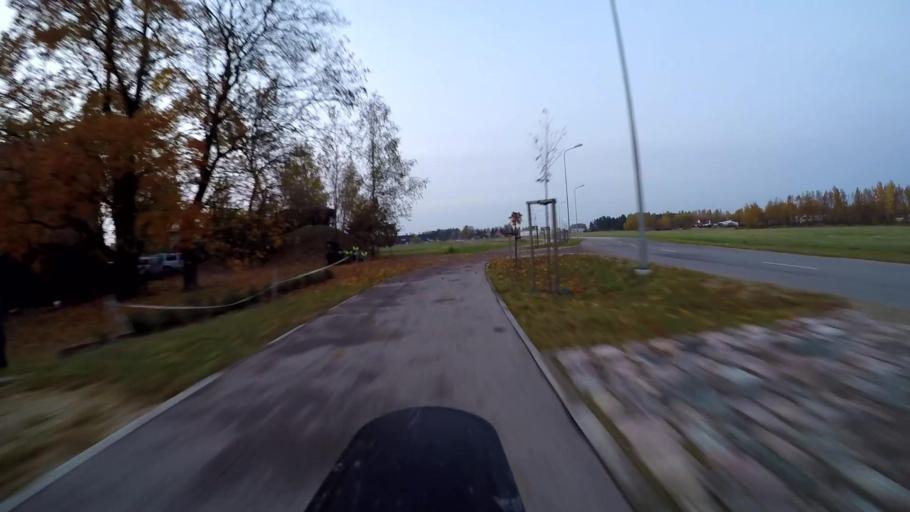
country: LV
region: Marupe
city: Marupe
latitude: 56.9126
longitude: 23.9954
